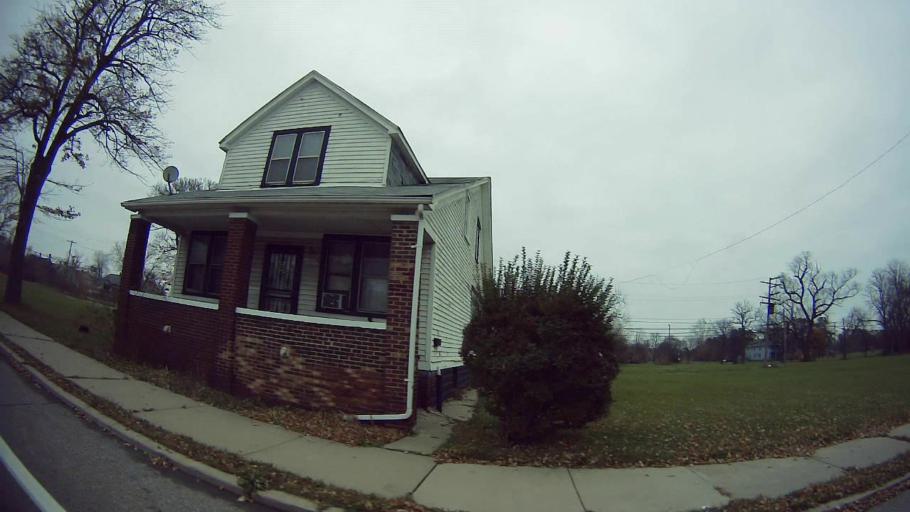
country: US
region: Michigan
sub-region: Wayne County
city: Hamtramck
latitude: 42.3639
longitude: -83.0440
